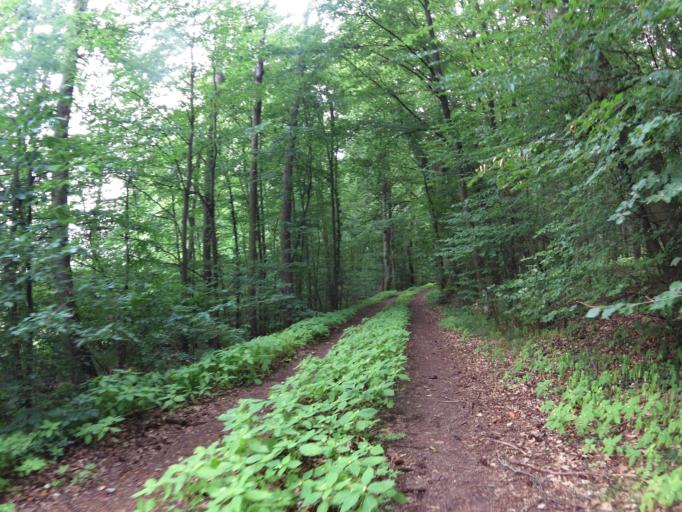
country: DE
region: Bavaria
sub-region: Regierungsbezirk Unterfranken
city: Geroldshausen
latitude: 49.7130
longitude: 9.8849
